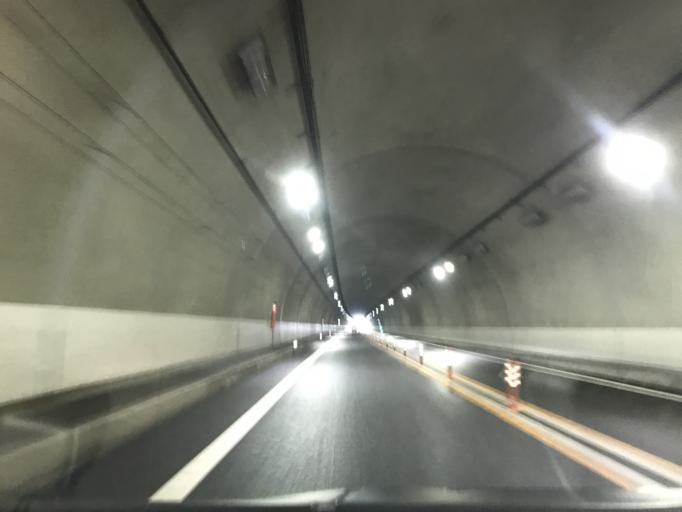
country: JP
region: Fukuoka
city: Nakatsu
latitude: 33.5140
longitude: 131.2795
